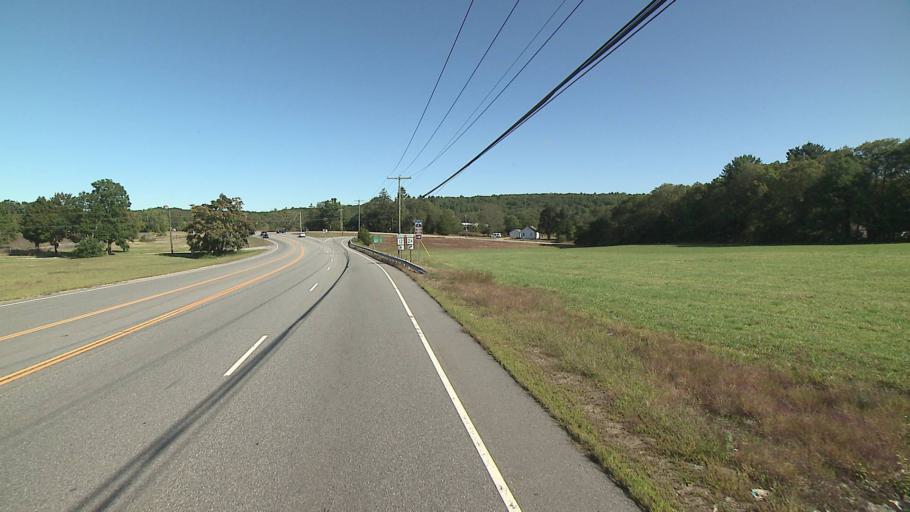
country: US
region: Connecticut
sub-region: New London County
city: Norwich
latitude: 41.4848
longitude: -72.0660
